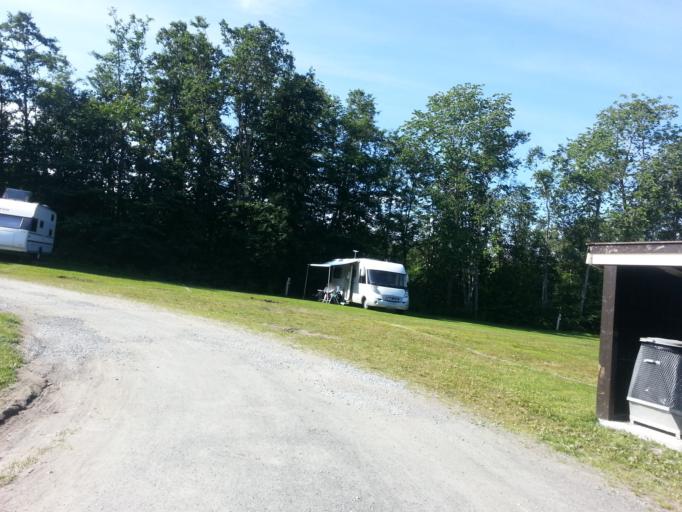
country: NO
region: Sor-Trondelag
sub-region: Malvik
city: Malvik
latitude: 63.4335
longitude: 10.7050
